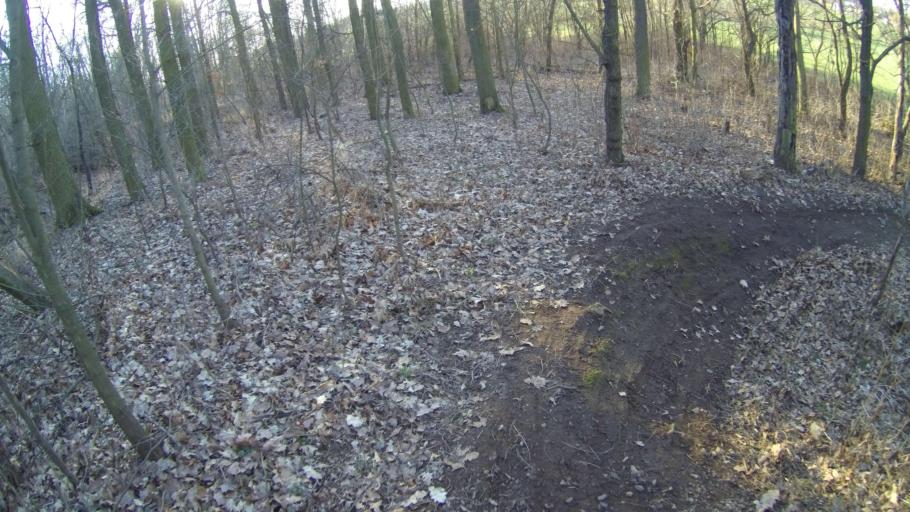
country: CZ
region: Central Bohemia
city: Neratovice
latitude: 50.2337
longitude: 14.5054
